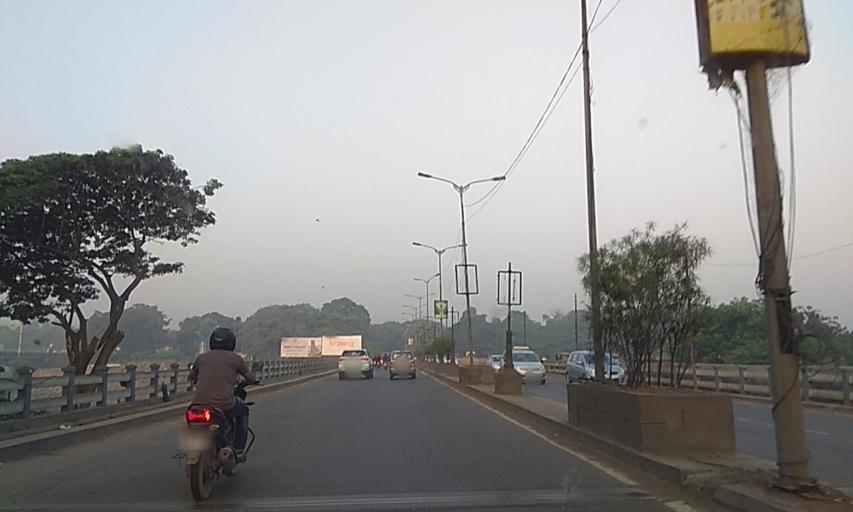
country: IN
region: Maharashtra
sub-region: Pune Division
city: Shivaji Nagar
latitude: 18.5297
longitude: 73.8616
